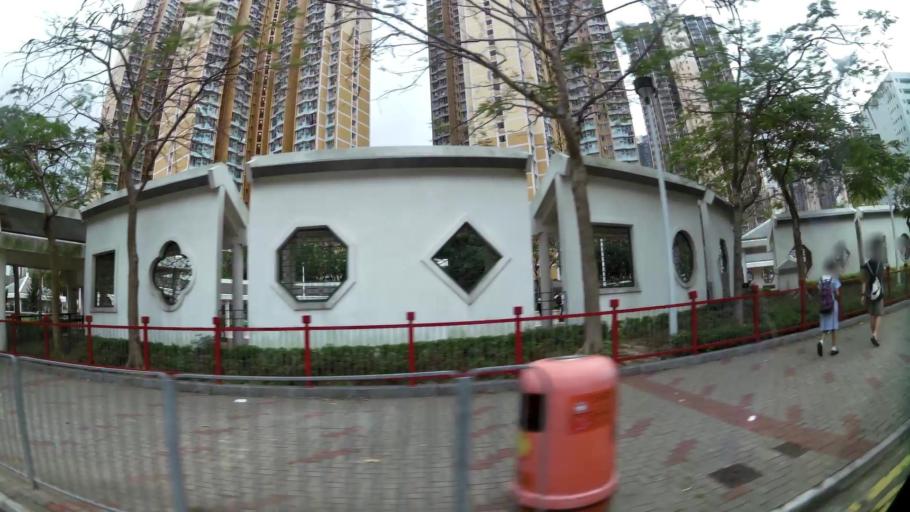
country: HK
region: Tsuen Wan
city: Tsuen Wan
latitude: 22.3675
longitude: 114.1306
